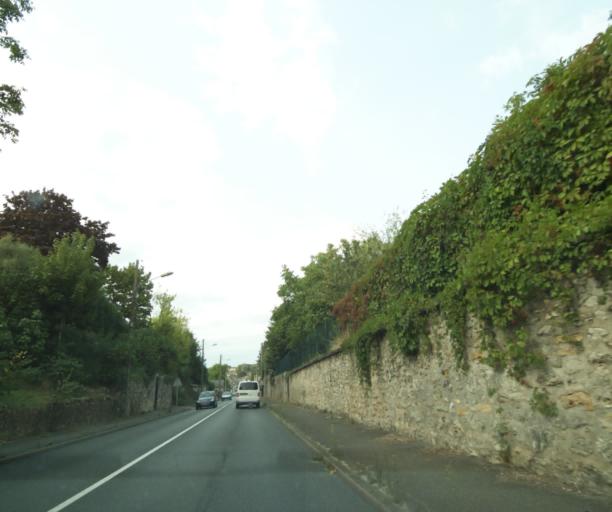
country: FR
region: Centre
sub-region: Departement d'Indre-et-Loire
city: Cormery
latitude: 47.2644
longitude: 0.8359
